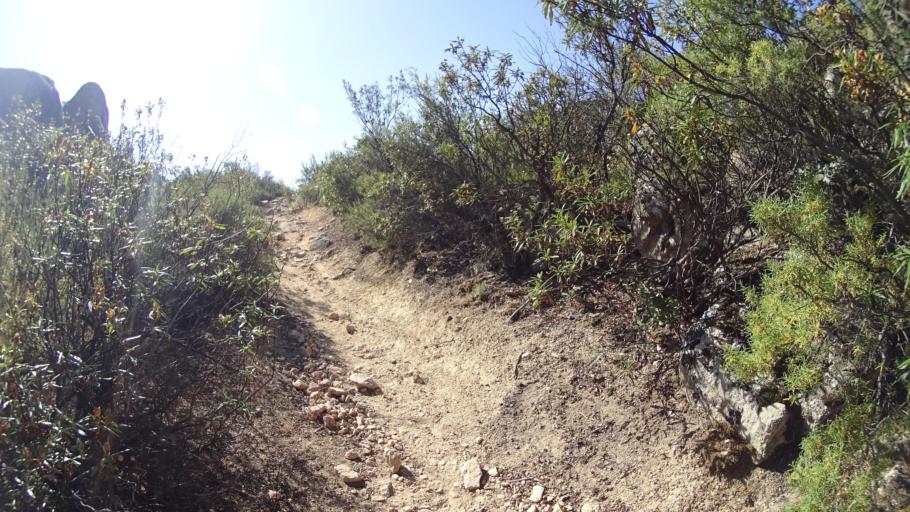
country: ES
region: Madrid
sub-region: Provincia de Madrid
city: Hoyo de Manzanares
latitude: 40.6415
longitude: -3.9358
